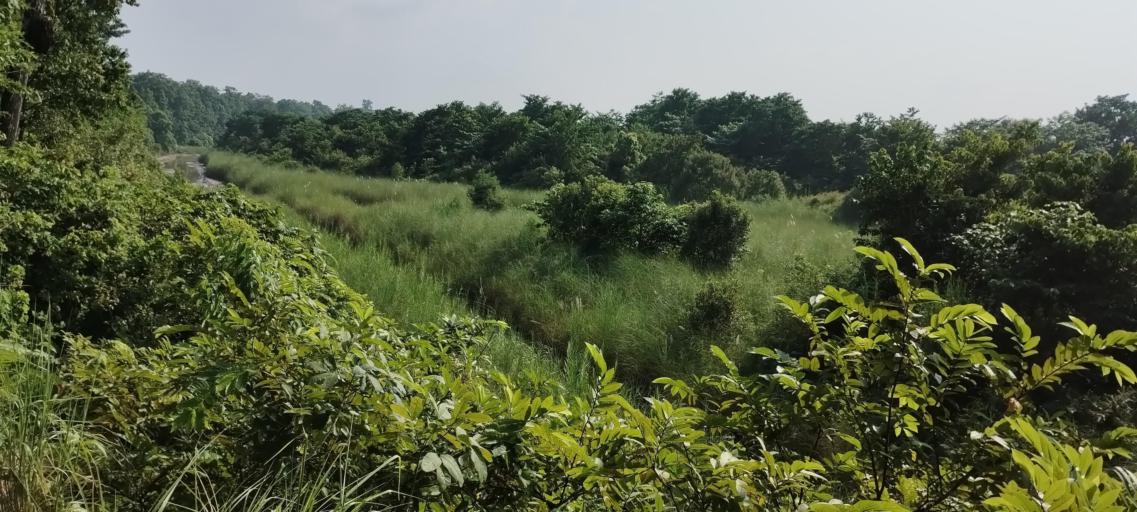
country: NP
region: Far Western
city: Tikapur
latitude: 28.5622
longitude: 81.2652
